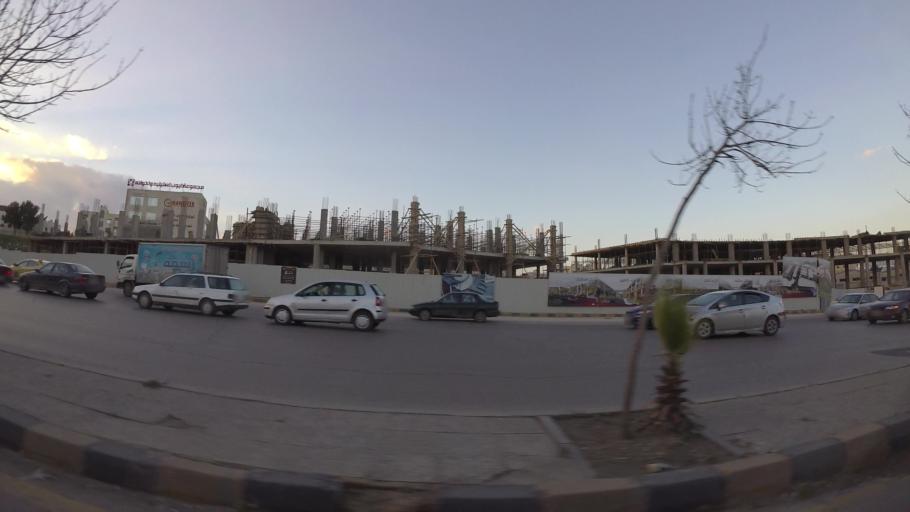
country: JO
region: Amman
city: Al Bunayyat ash Shamaliyah
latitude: 31.9182
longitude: 35.9063
